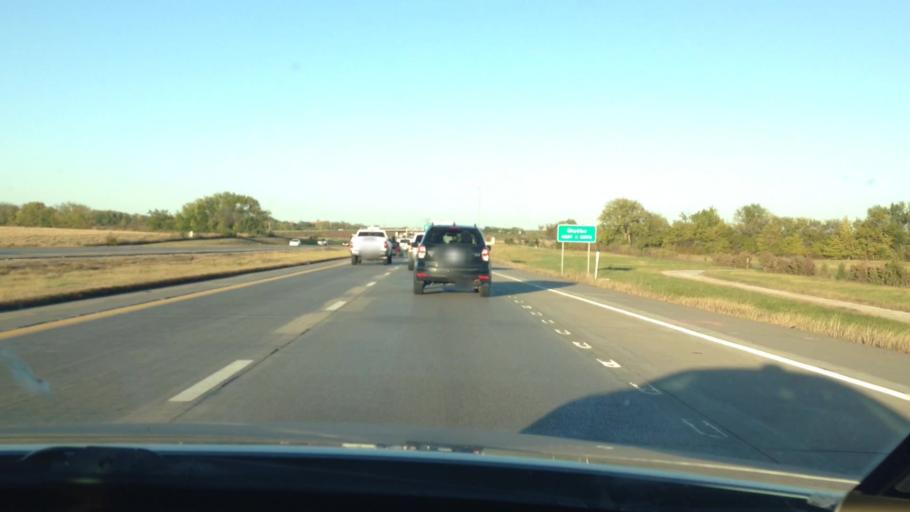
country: US
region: Kansas
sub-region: Johnson County
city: Olathe
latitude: 38.8341
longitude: -94.8486
